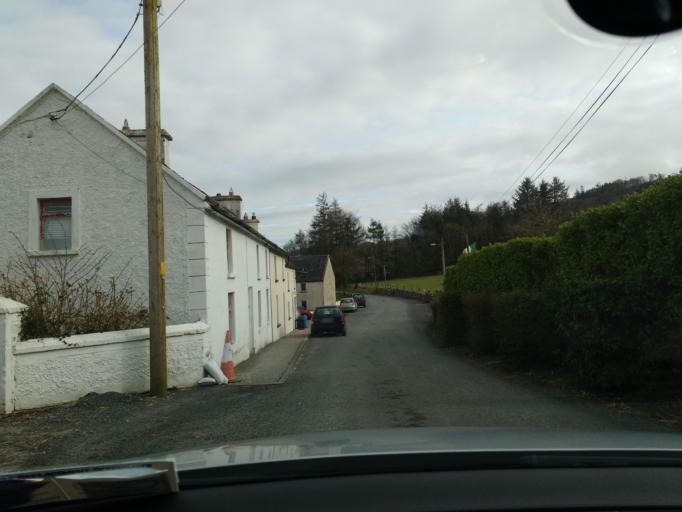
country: IE
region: Leinster
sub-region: Kilkenny
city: Callan
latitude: 52.6574
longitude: -7.5461
